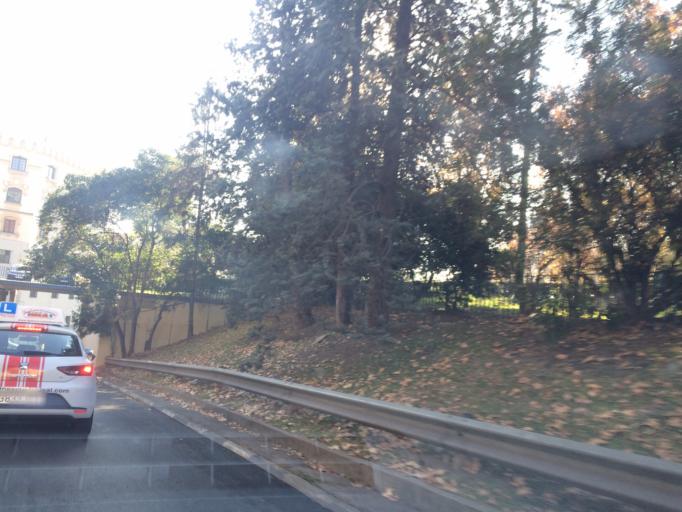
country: ES
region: Madrid
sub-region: Provincia de Madrid
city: City Center
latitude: 40.4237
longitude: -3.7152
